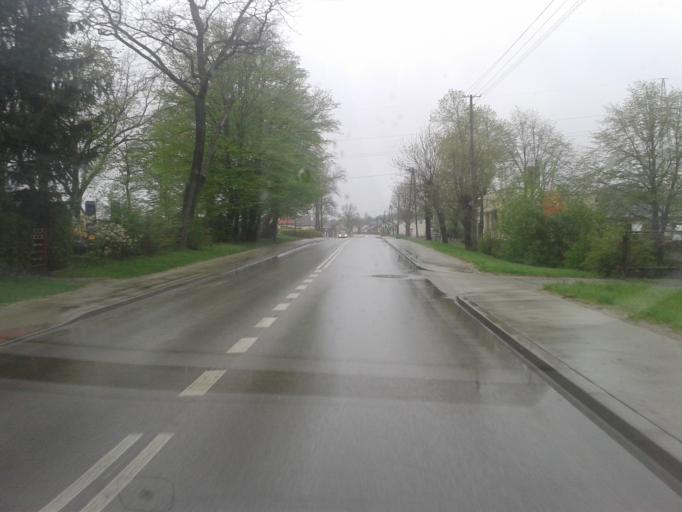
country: PL
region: Lublin Voivodeship
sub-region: Powiat tomaszowski
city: Belzec
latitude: 50.3832
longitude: 23.4219
